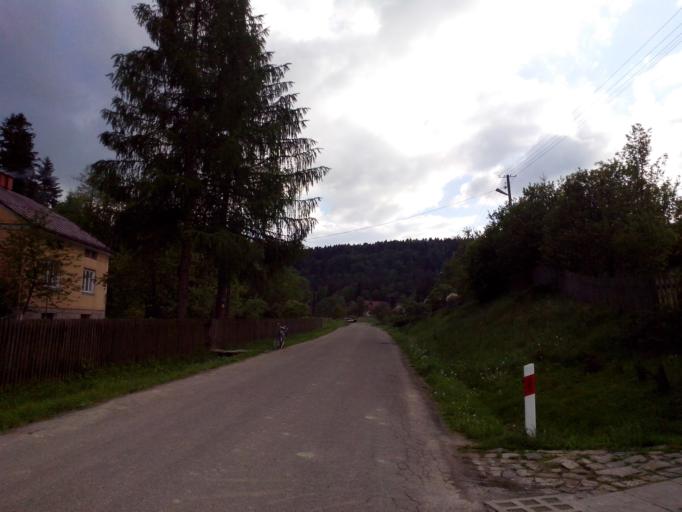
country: PL
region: Subcarpathian Voivodeship
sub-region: Powiat strzyzowski
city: Strzyzow
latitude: 49.8129
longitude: 21.8300
